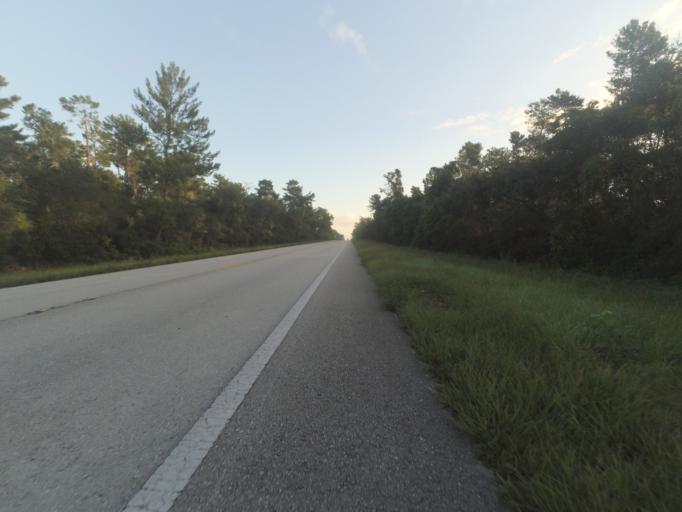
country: US
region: Florida
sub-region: Lake County
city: Astor
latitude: 29.2600
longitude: -81.6464
